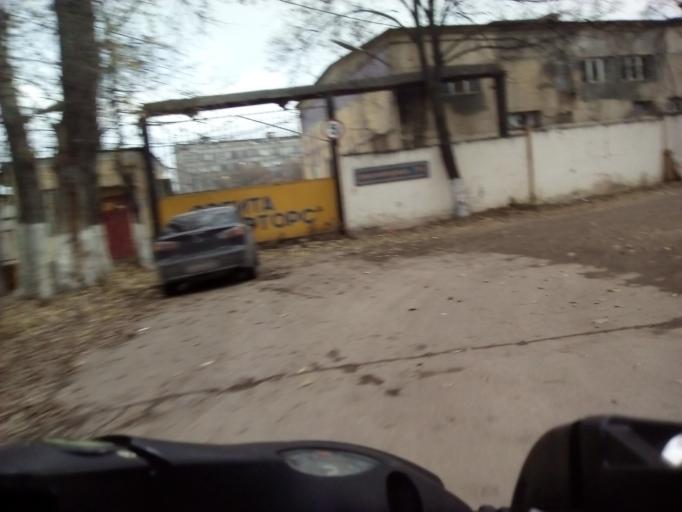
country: RU
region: Moscow
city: Lefortovo
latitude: 55.7604
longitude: 37.7171
